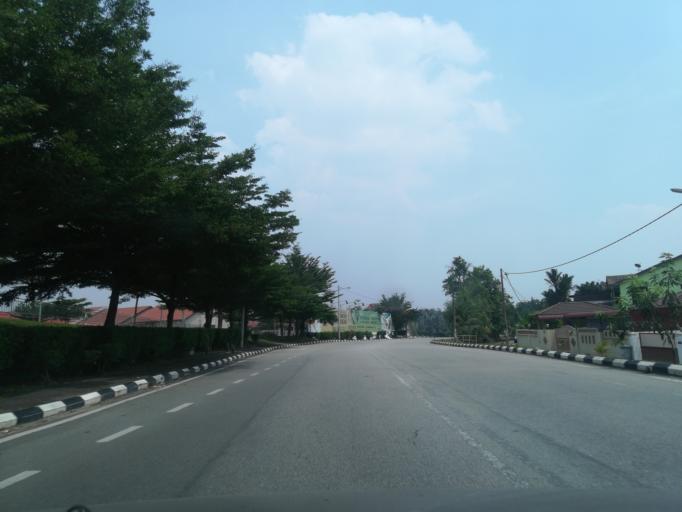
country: MY
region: Kedah
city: Kulim
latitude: 5.3989
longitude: 100.5677
